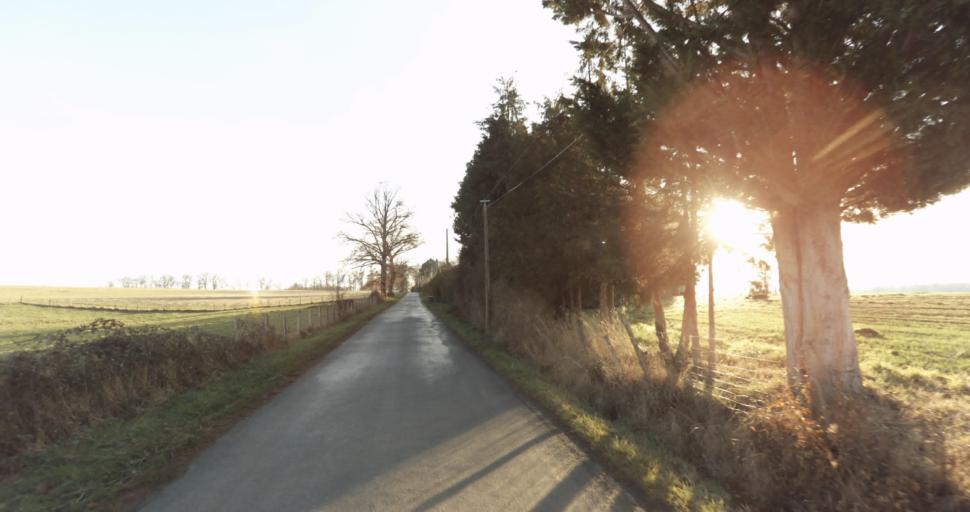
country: FR
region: Limousin
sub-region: Departement de la Haute-Vienne
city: Aixe-sur-Vienne
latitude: 45.7836
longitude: 1.1415
